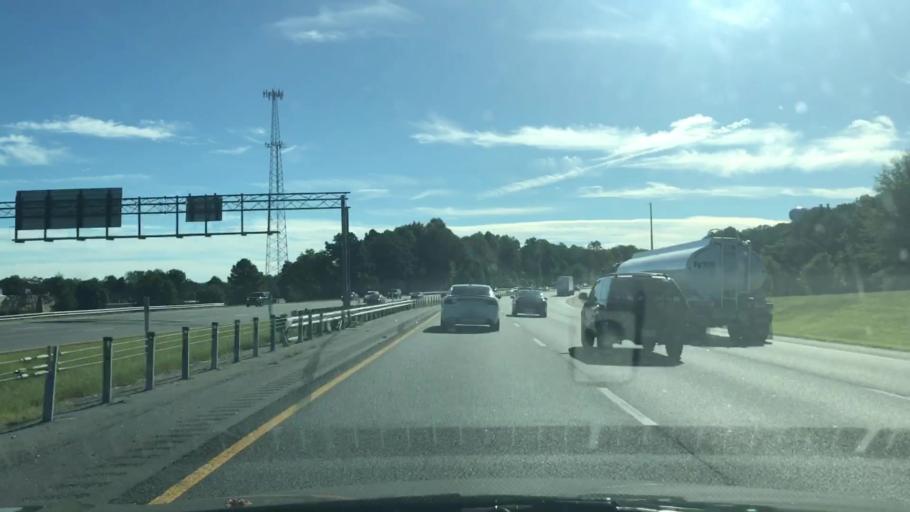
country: US
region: Georgia
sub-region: DeKalb County
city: Tucker
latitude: 33.8349
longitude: -84.1985
